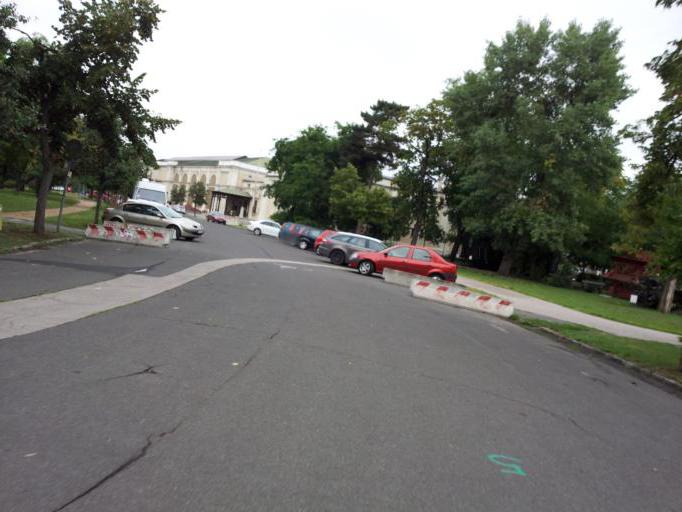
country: HU
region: Budapest
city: Budapest XIV. keruelet
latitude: 47.5127
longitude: 19.0925
